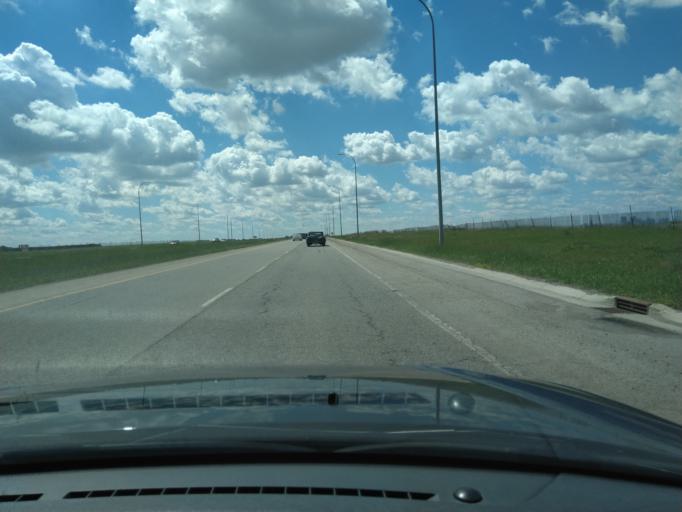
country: CA
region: Alberta
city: Calgary
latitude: 51.1463
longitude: -113.9702
